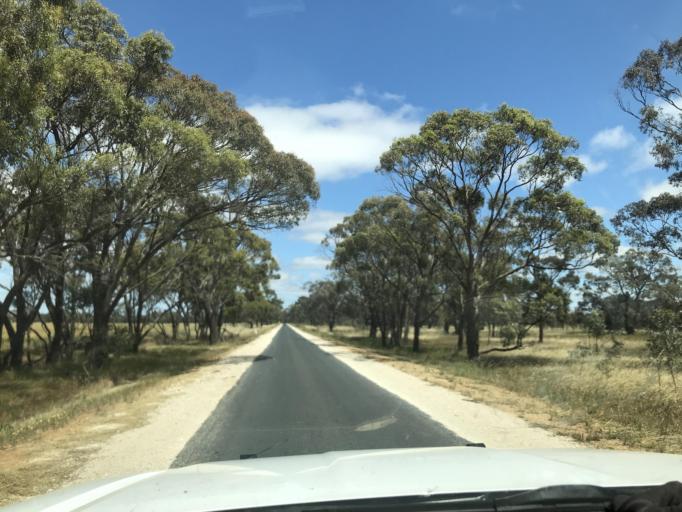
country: AU
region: South Australia
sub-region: Tatiara
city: Bordertown
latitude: -36.3086
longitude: 141.0488
